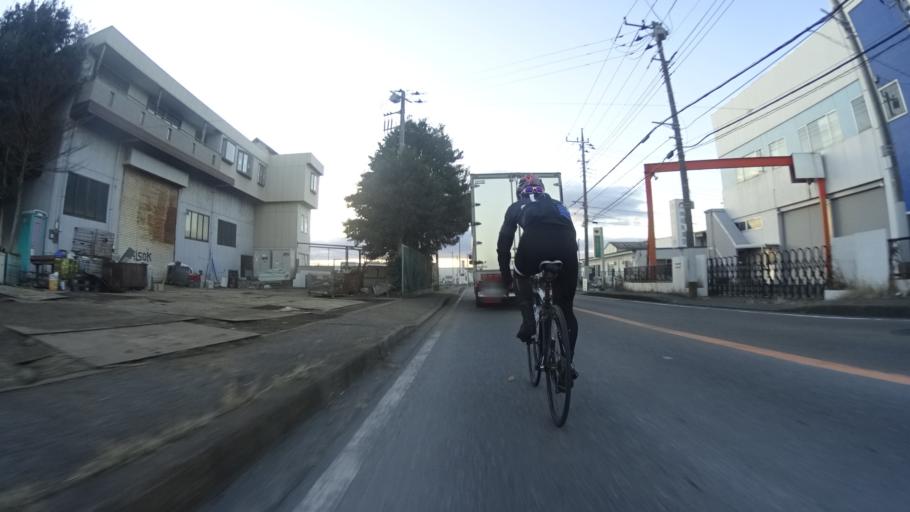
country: JP
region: Kanagawa
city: Zama
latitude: 35.5458
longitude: 139.3599
